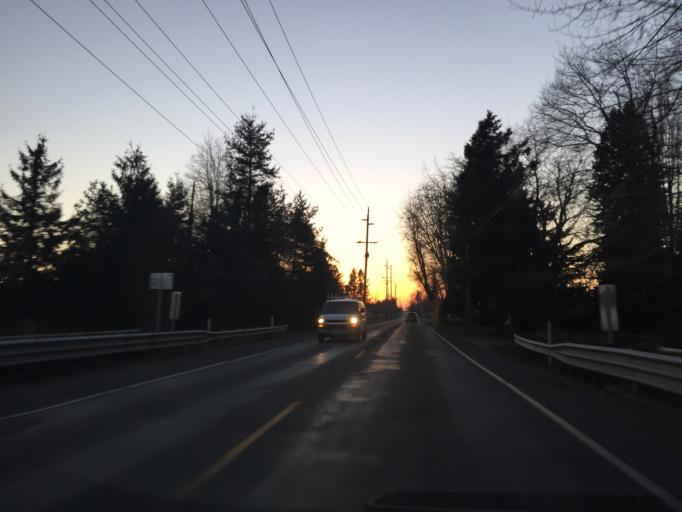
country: US
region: Washington
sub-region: Whatcom County
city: Nooksack
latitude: 48.9639
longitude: -122.3275
